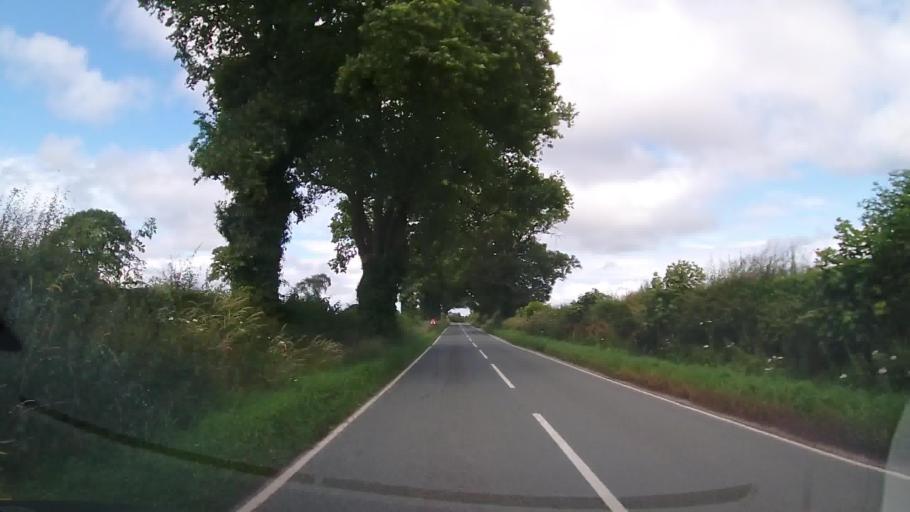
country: GB
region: England
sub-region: Shropshire
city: Great Ness
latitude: 52.7954
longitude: -2.9602
